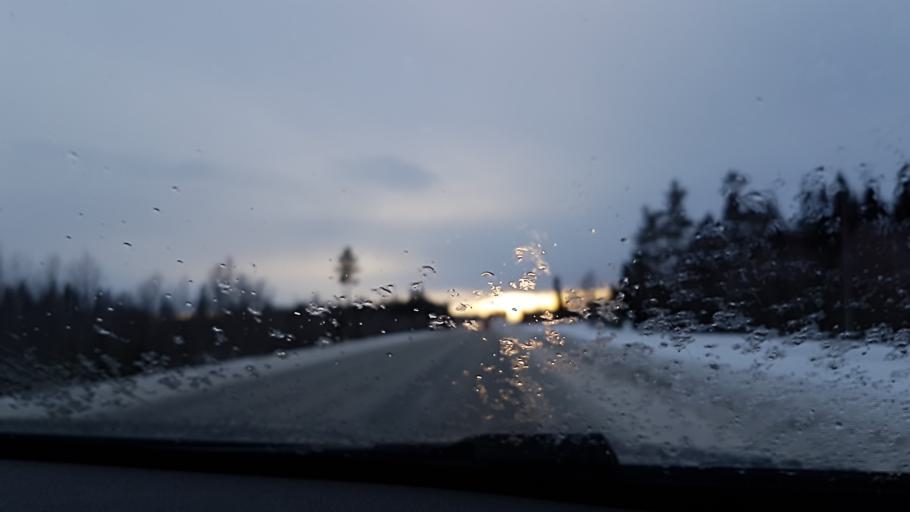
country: SE
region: Jaemtland
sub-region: Bergs Kommun
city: Hoverberg
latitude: 62.7084
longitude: 14.4113
